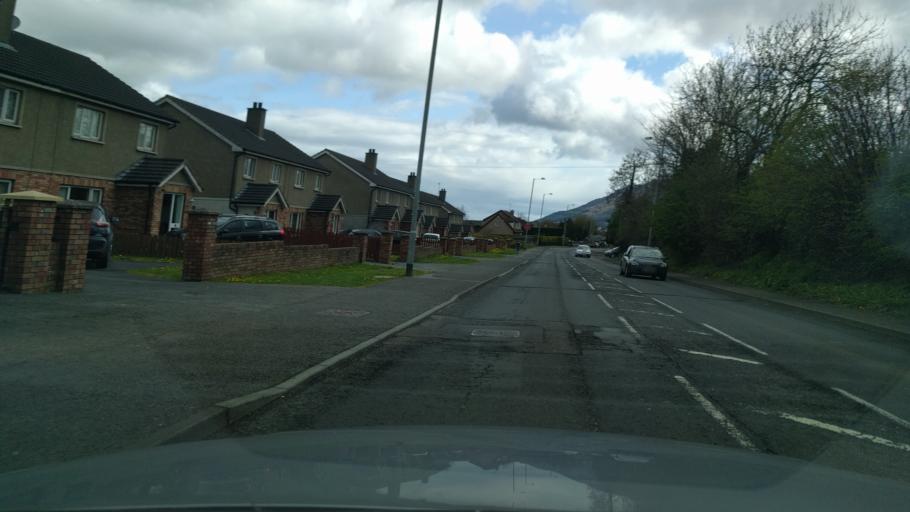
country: GB
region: Northern Ireland
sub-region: Down District
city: Warrenpoint
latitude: 54.1074
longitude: -6.2534
